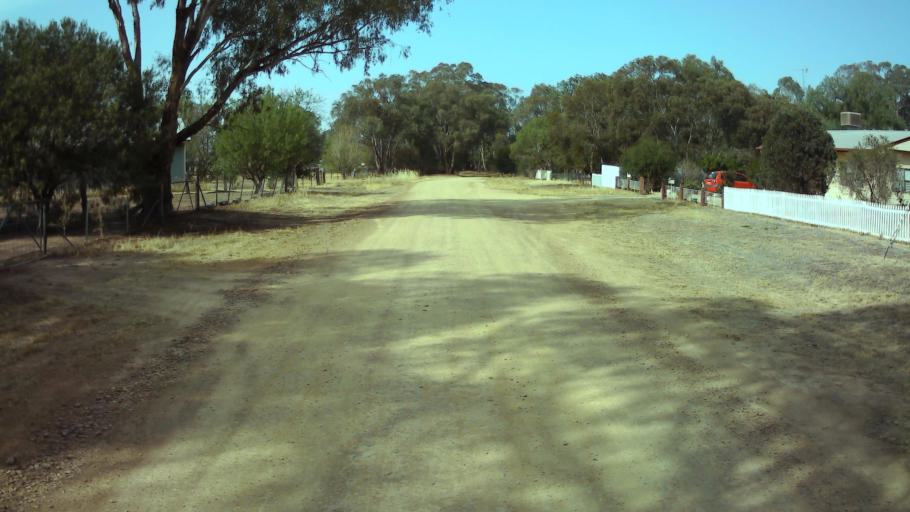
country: AU
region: New South Wales
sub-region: Weddin
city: Grenfell
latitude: -33.8974
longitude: 148.1518
